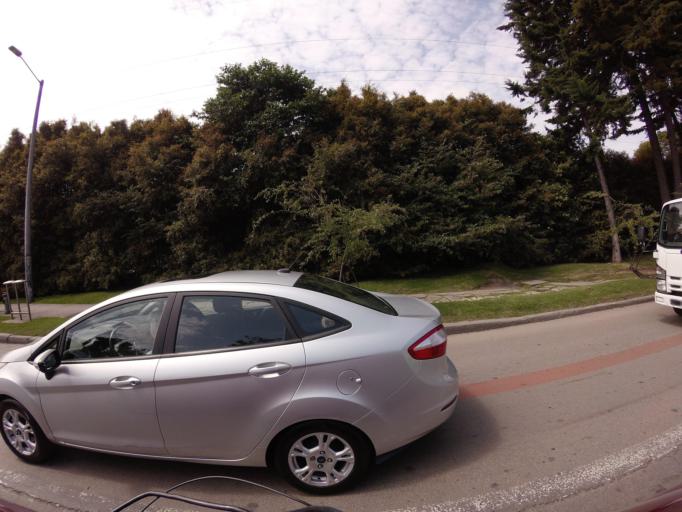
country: CO
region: Bogota D.C.
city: Barrio San Luis
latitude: 4.7024
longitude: -74.0816
